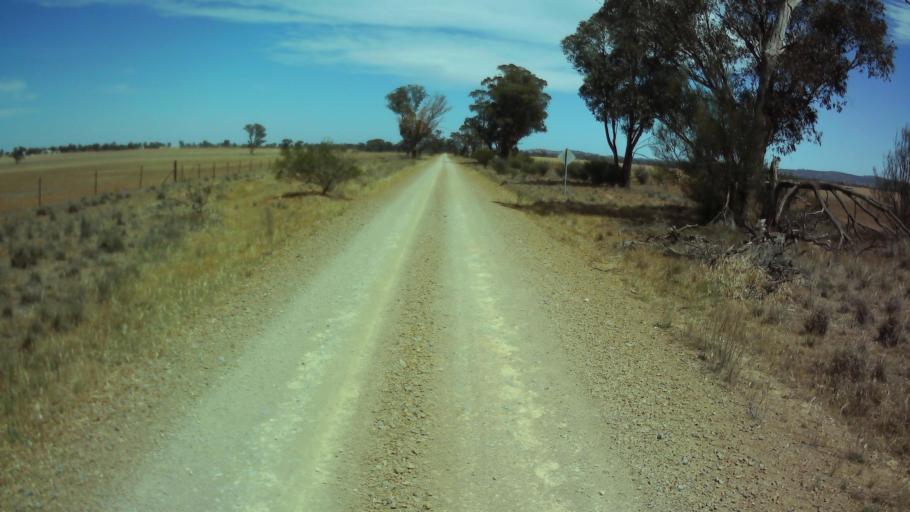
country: AU
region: New South Wales
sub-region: Weddin
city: Grenfell
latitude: -33.8589
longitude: 147.9258
